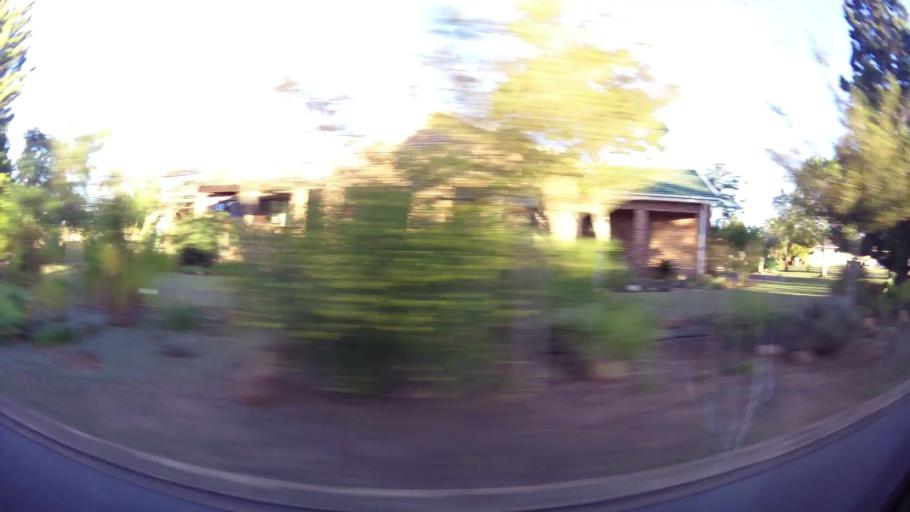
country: ZA
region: Western Cape
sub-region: Eden District Municipality
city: Riversdale
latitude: -34.0821
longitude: 21.2418
